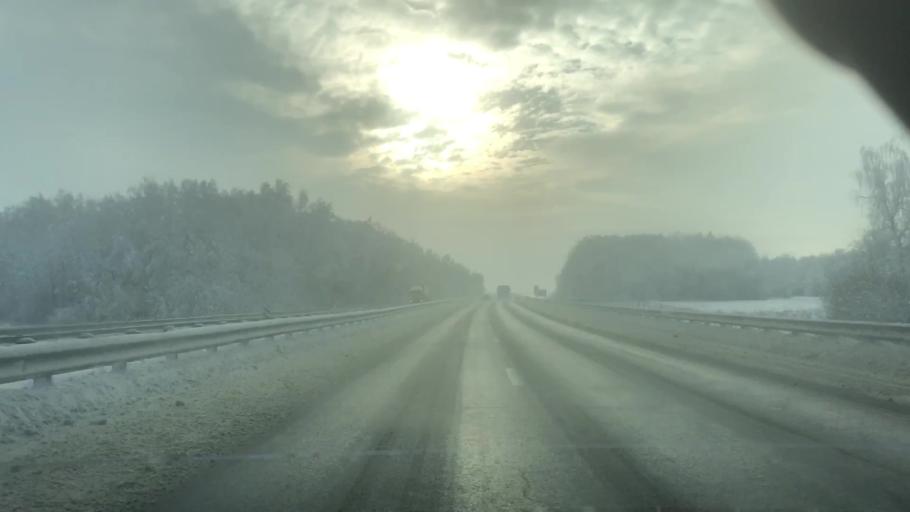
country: RU
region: Tula
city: Venev
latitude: 54.3829
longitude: 38.1546
